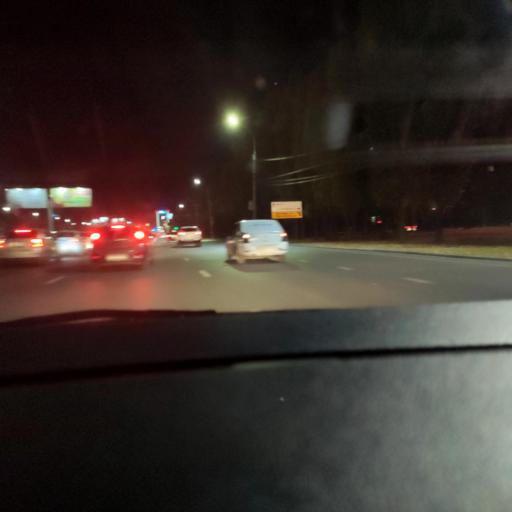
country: RU
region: Voronezj
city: Podgornoye
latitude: 51.7123
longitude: 39.1803
